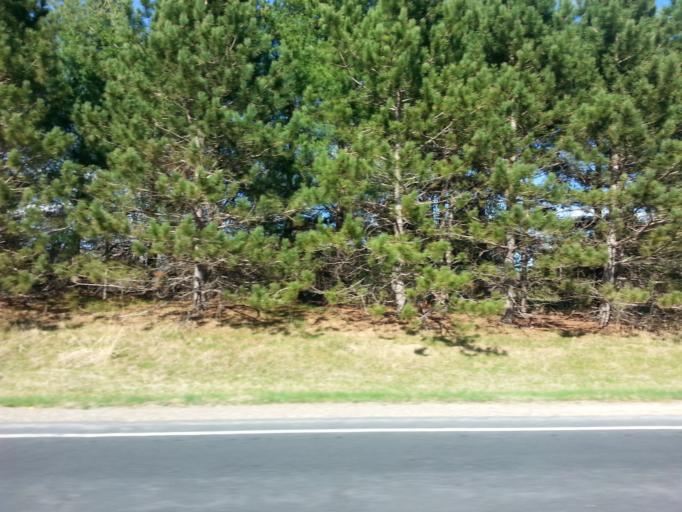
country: US
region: Minnesota
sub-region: Washington County
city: Bayport
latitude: 45.0549
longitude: -92.7256
